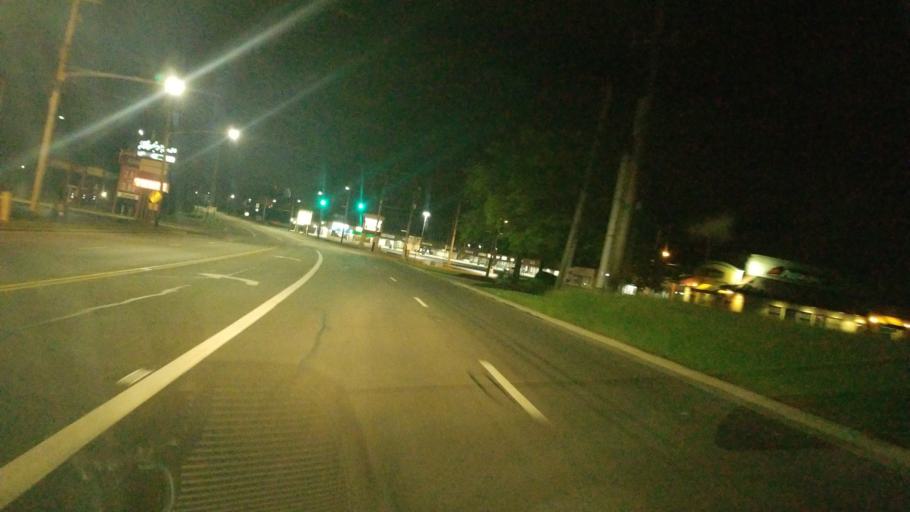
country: US
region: Ohio
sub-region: Trumbull County
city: McKinley Heights
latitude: 41.1963
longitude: -80.7281
